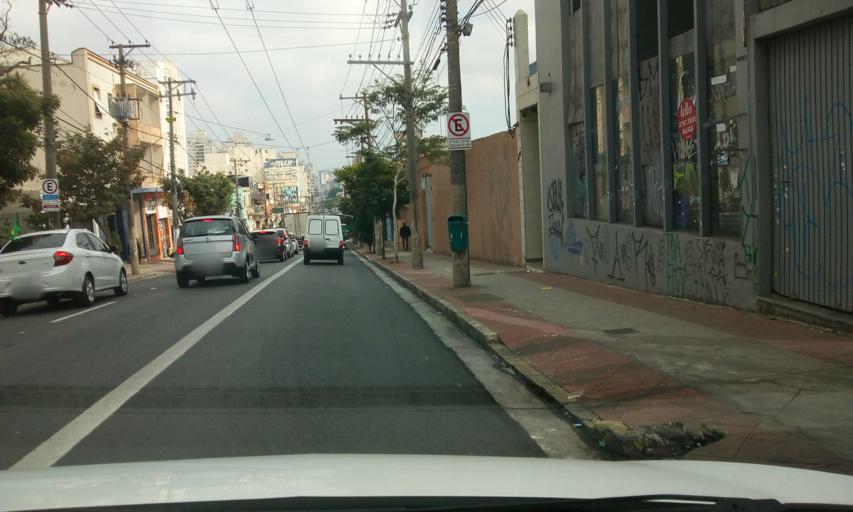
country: BR
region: Sao Paulo
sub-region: Sao Paulo
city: Sao Paulo
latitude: -23.5557
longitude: -46.5981
